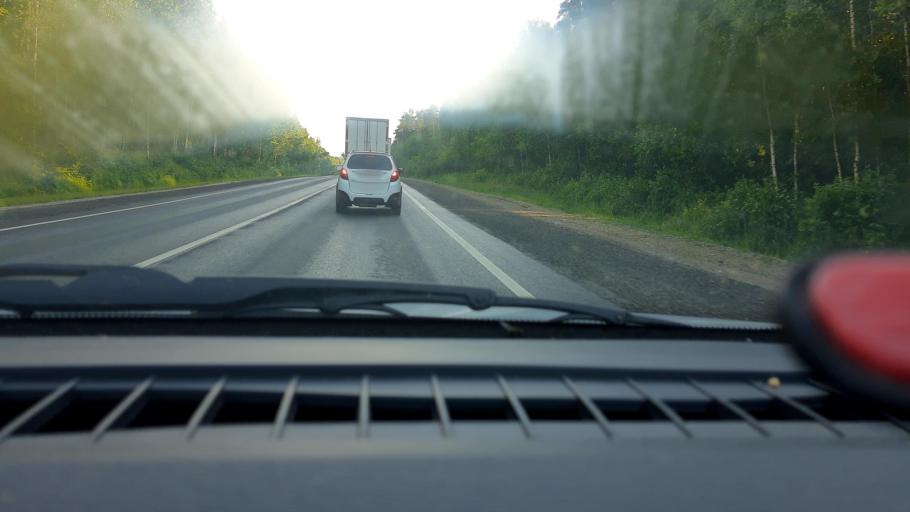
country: RU
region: Nizjnij Novgorod
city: Arzamas
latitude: 55.5080
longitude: 43.8966
